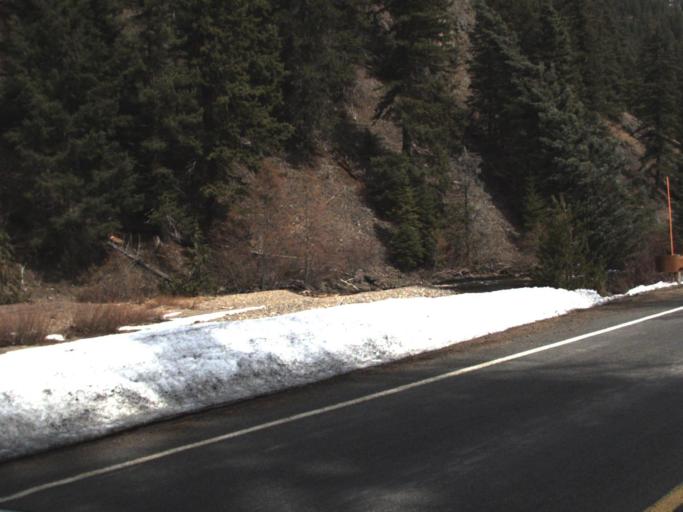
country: US
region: Washington
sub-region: Kittitas County
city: Cle Elum
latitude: 46.9658
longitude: -121.2591
